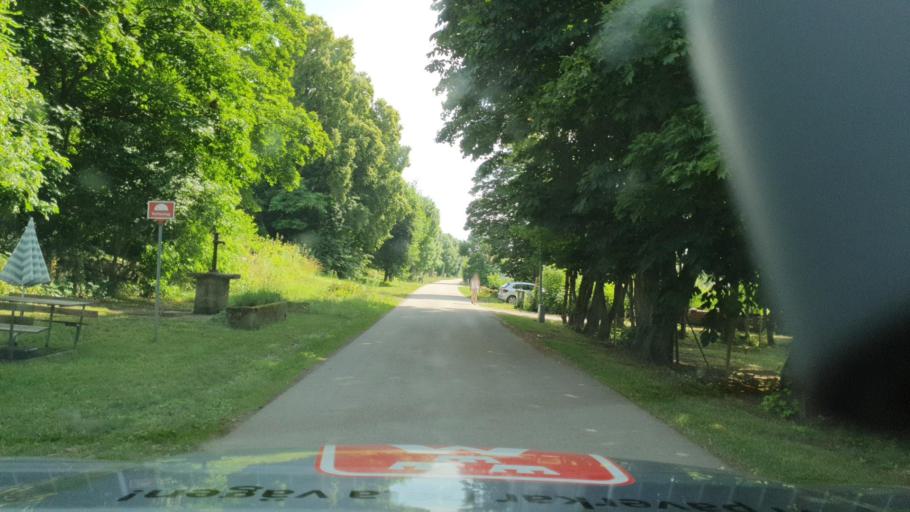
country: SE
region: Kalmar
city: Faerjestaden
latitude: 56.5954
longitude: 16.4664
